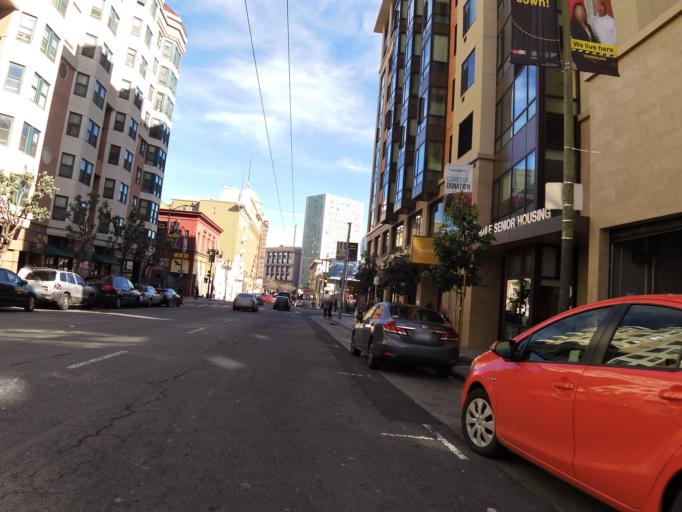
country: US
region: California
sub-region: San Francisco County
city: San Francisco
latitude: 37.7820
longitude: -122.4129
